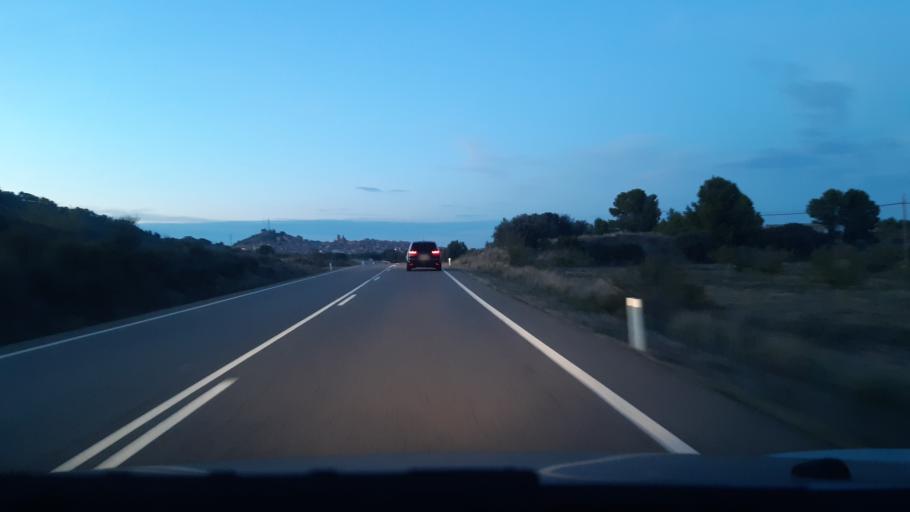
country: ES
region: Aragon
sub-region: Provincia de Teruel
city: Calaceite
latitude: 41.0023
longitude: 0.1933
